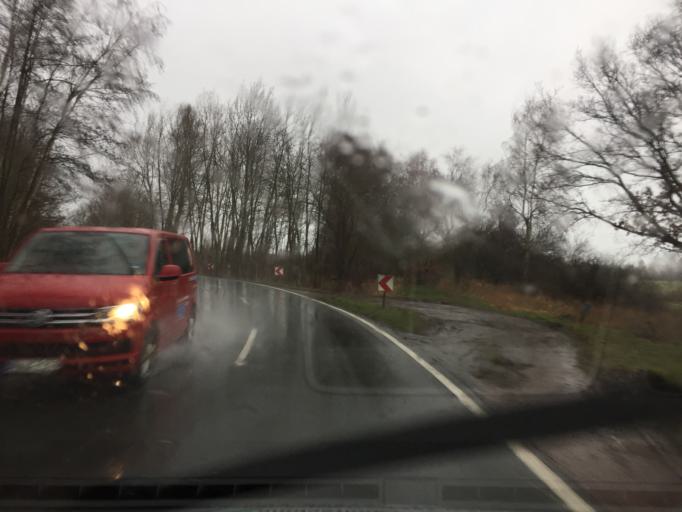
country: DE
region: Lower Saxony
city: Maasen
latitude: 52.6370
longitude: 8.8907
